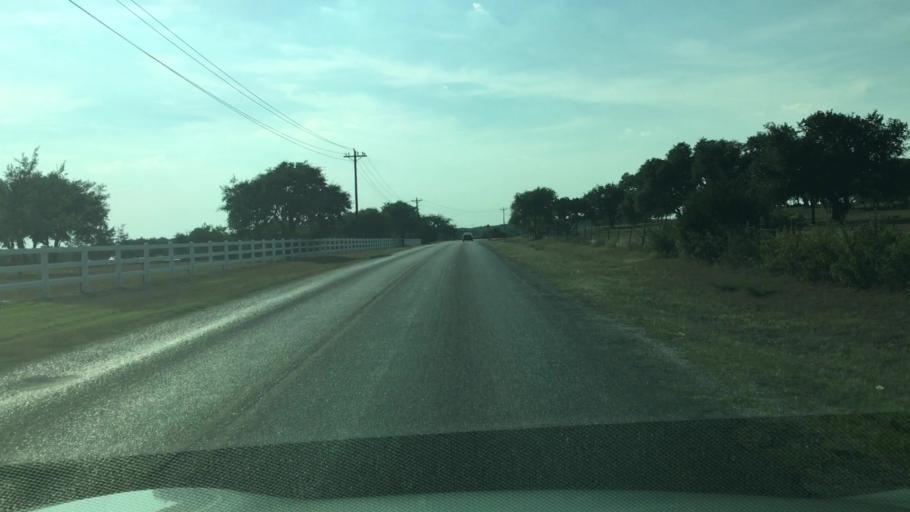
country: US
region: Texas
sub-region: Hays County
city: Dripping Springs
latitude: 30.1492
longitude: -97.9911
